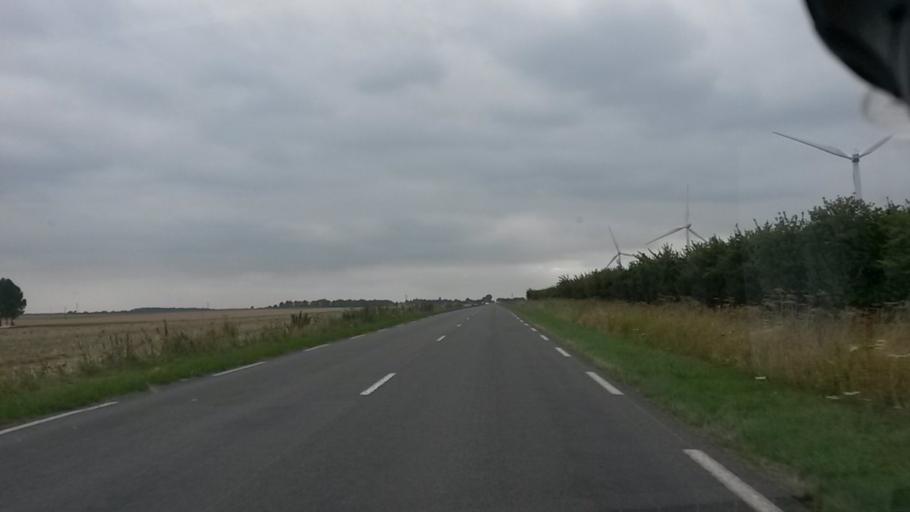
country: FR
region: Haute-Normandie
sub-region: Departement de la Seine-Maritime
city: Aumale
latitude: 49.7706
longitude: 1.8295
